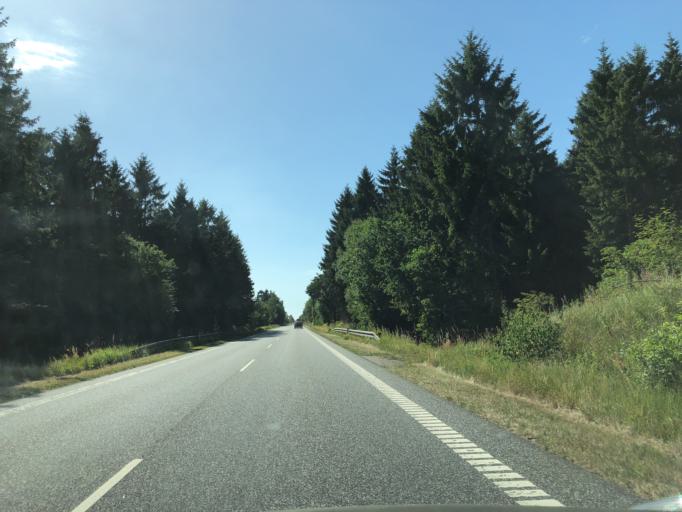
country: DK
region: North Denmark
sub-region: Vesthimmerland Kommune
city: Alestrup
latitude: 56.6115
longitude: 9.4098
